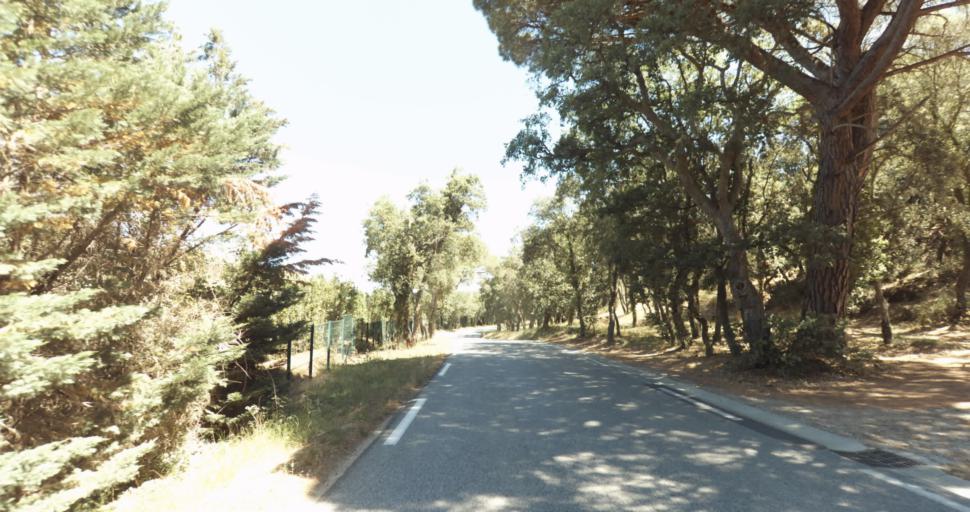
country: FR
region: Provence-Alpes-Cote d'Azur
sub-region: Departement du Var
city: Gassin
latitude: 43.2499
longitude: 6.5813
